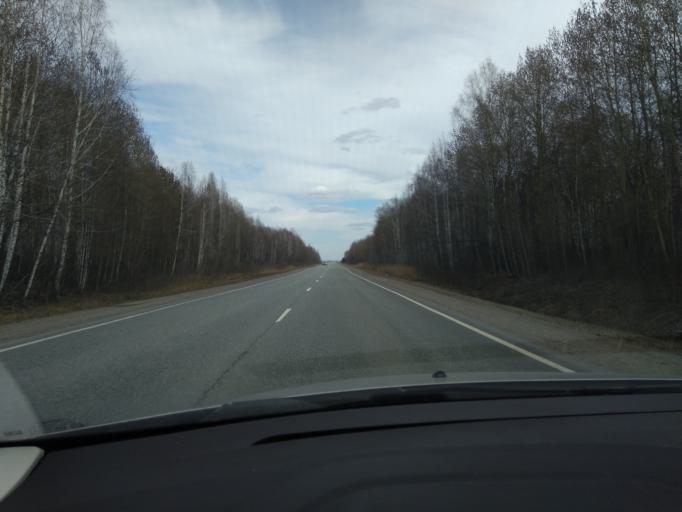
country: RU
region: Sverdlovsk
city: Yelanskiy
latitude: 56.7660
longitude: 62.4228
